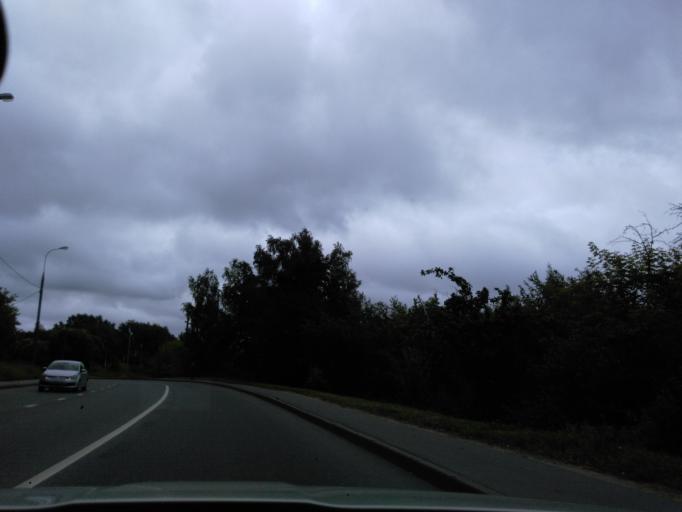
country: RU
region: Moscow
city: Zelenograd
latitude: 55.9720
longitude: 37.1821
